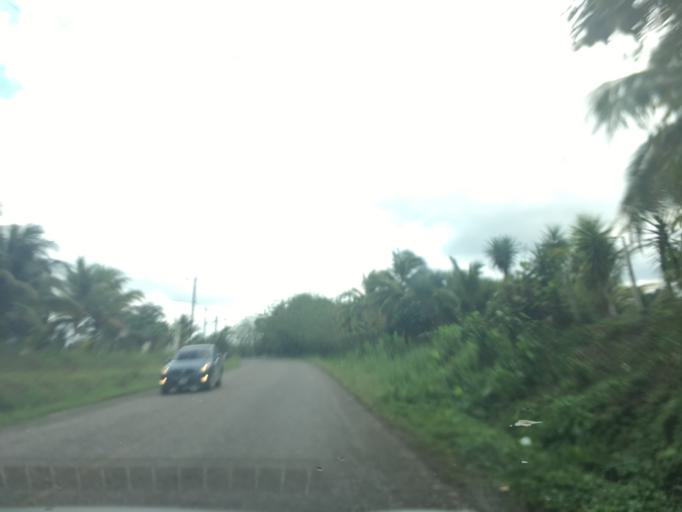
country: BZ
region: Stann Creek
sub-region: Dangriga
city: Dangriga
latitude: 16.9984
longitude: -88.4156
